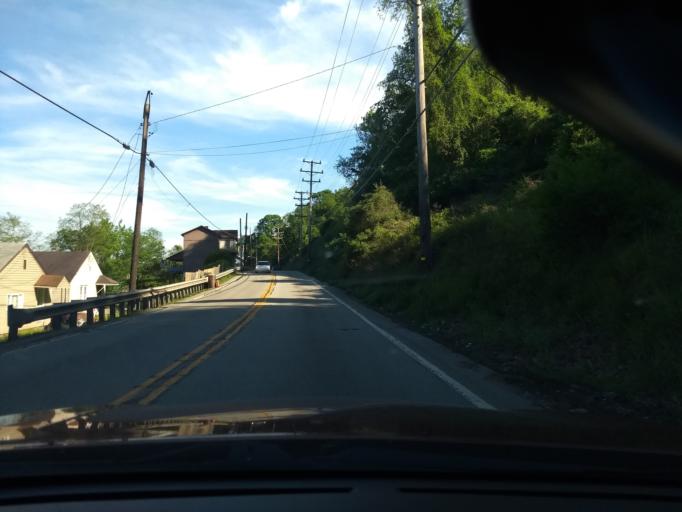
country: US
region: Pennsylvania
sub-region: Allegheny County
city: Wilson
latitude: 40.3164
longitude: -79.8979
